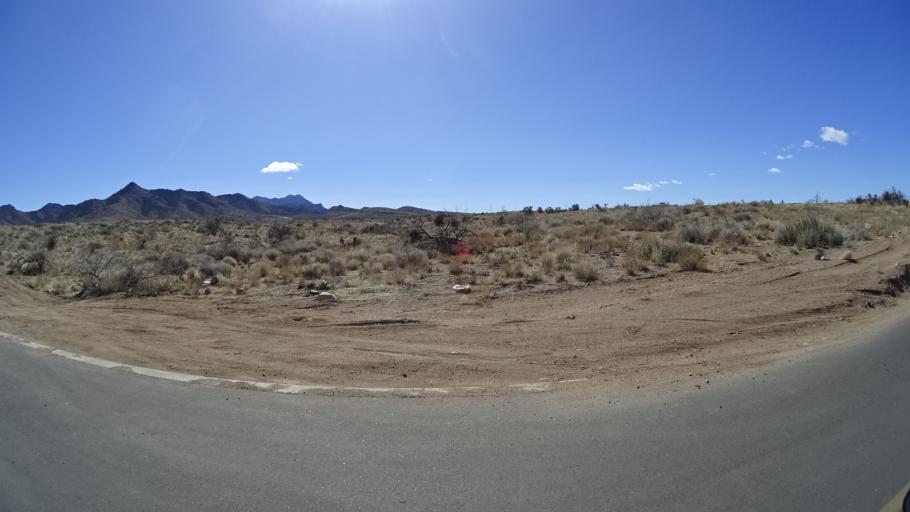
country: US
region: Arizona
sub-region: Mohave County
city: Kingman
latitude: 35.1963
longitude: -113.9633
